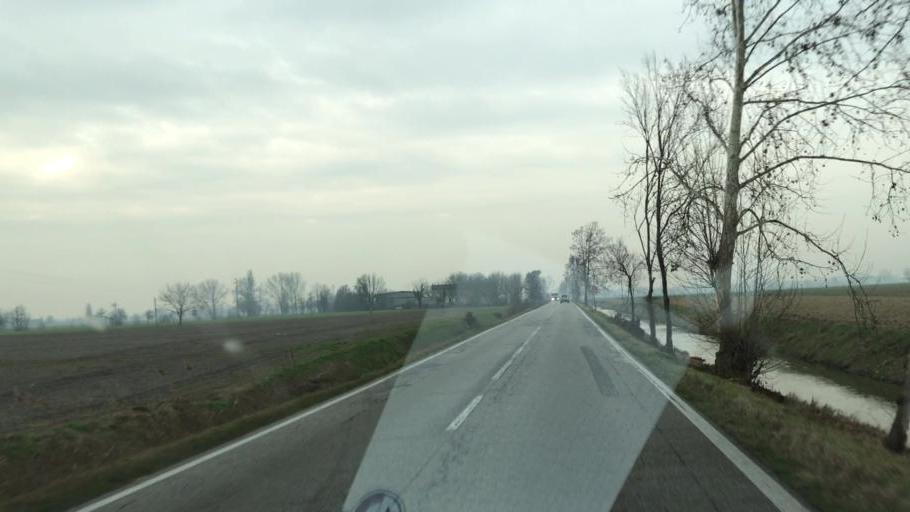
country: IT
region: Lombardy
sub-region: Provincia di Mantova
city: Casalmoro
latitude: 45.2425
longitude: 10.4159
